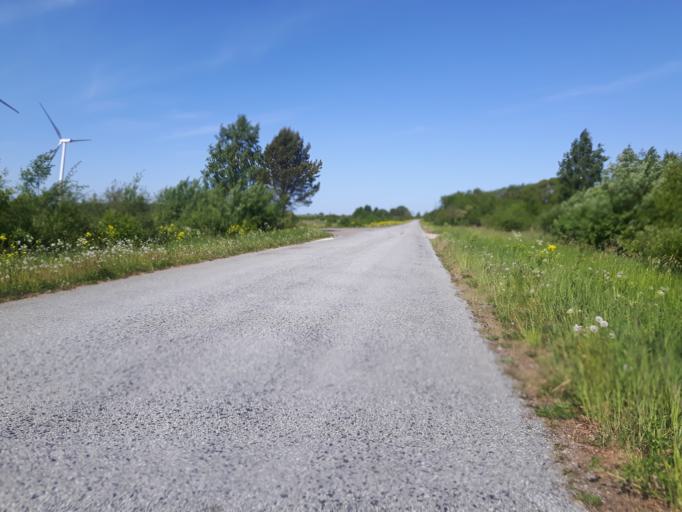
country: EE
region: Ida-Virumaa
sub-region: Aseri vald
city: Aseri
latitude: 59.4609
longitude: 26.8326
